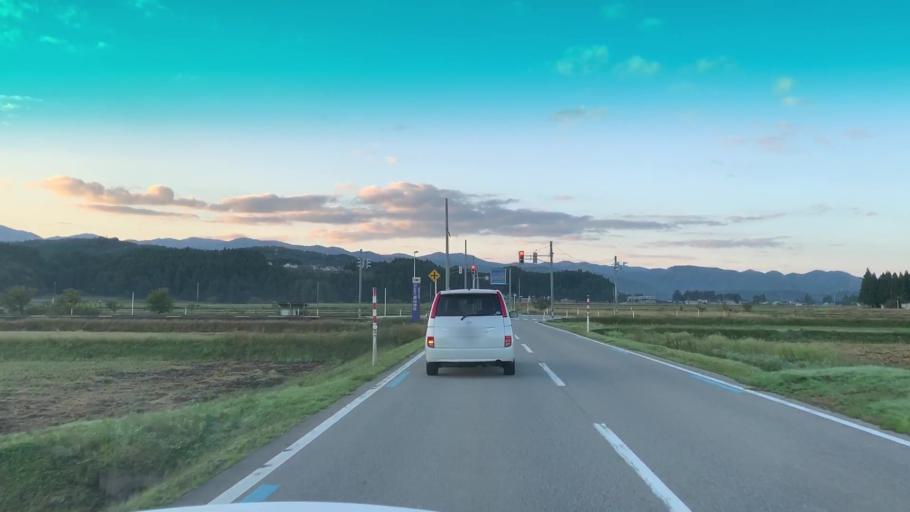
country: JP
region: Toyama
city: Kamiichi
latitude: 36.6263
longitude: 137.3286
